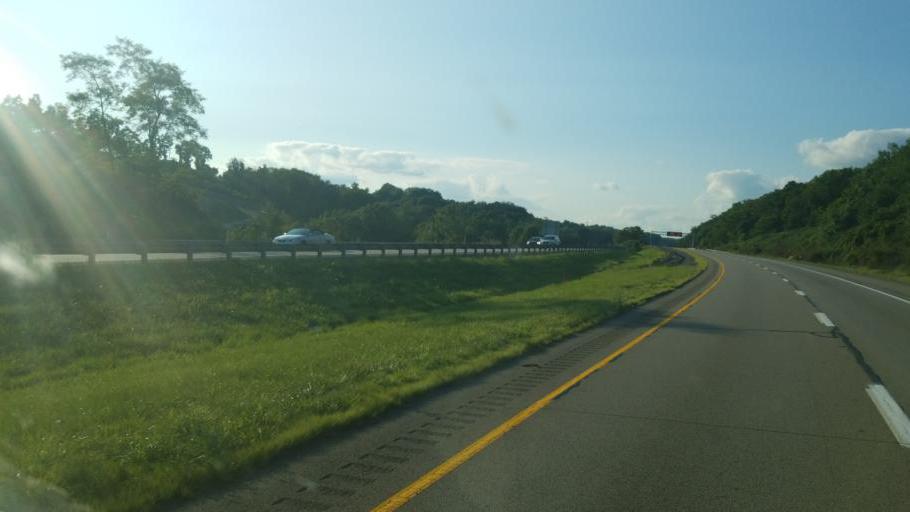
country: US
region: Pennsylvania
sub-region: Allegheny County
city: McKees Rocks
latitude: 40.4658
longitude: -80.1119
